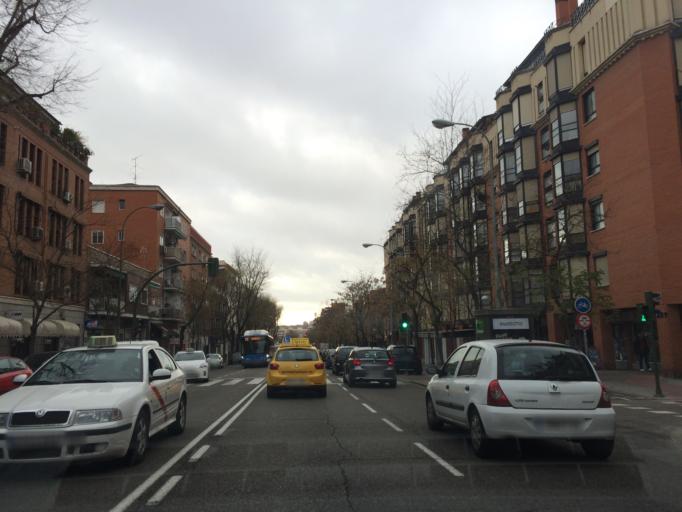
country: ES
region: Madrid
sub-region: Provincia de Madrid
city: Madrid
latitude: 40.4133
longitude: -3.7172
